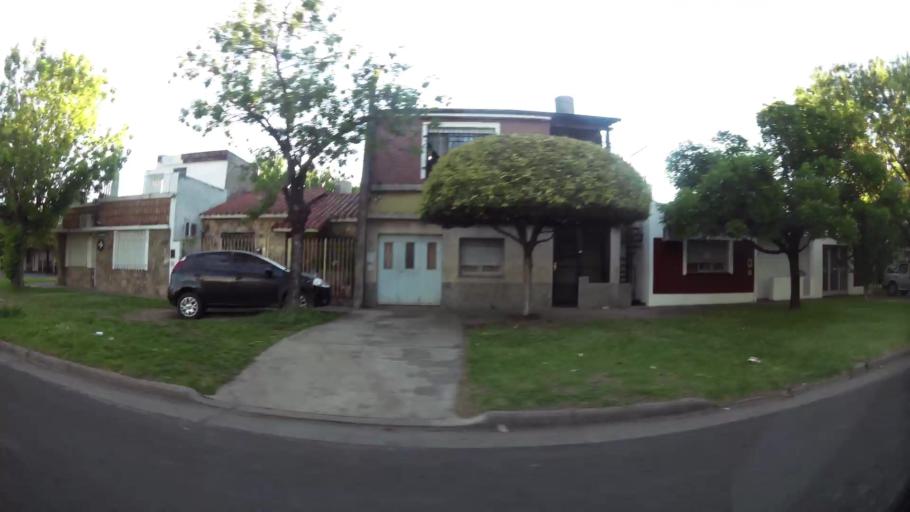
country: AR
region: Santa Fe
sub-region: Departamento de Rosario
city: Rosario
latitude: -32.9725
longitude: -60.6698
